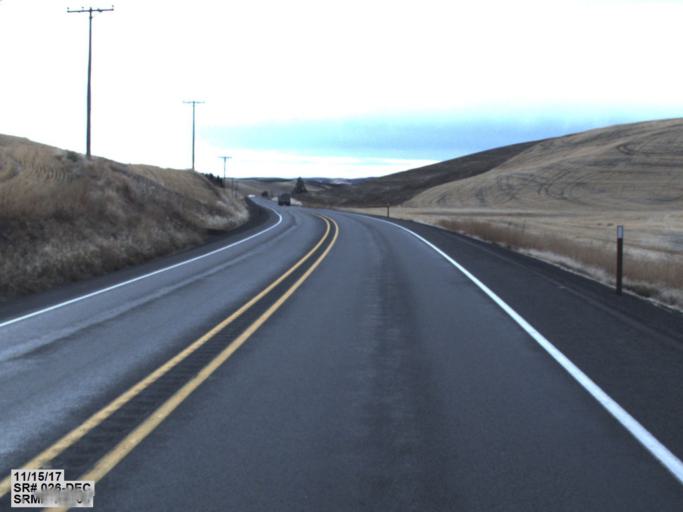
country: US
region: Washington
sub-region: Whitman County
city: Colfax
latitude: 46.8572
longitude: -117.4607
